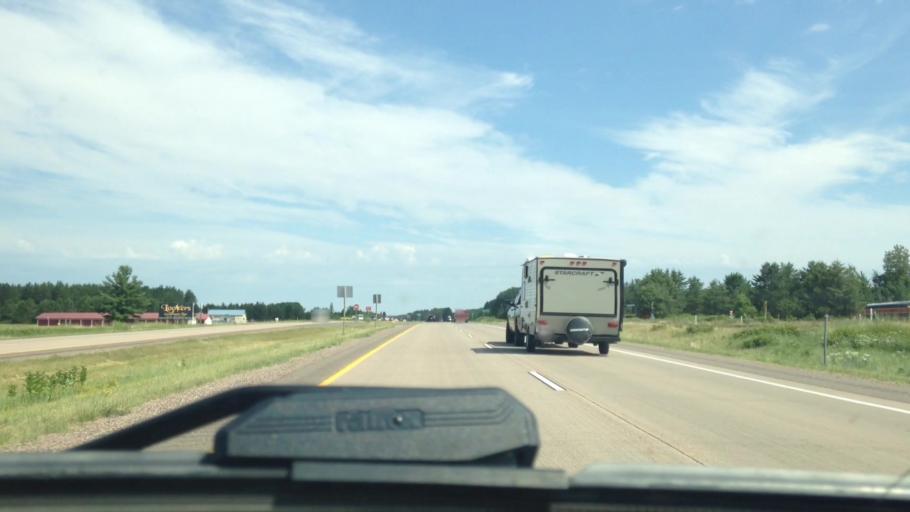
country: US
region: Wisconsin
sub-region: Washburn County
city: Spooner
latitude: 45.8778
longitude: -91.8291
